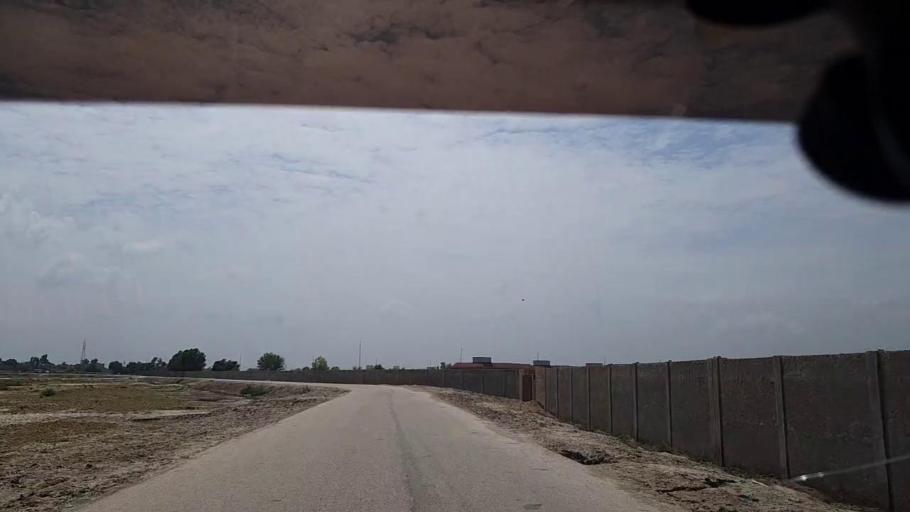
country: PK
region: Sindh
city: Ghauspur
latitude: 28.0935
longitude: 68.9596
